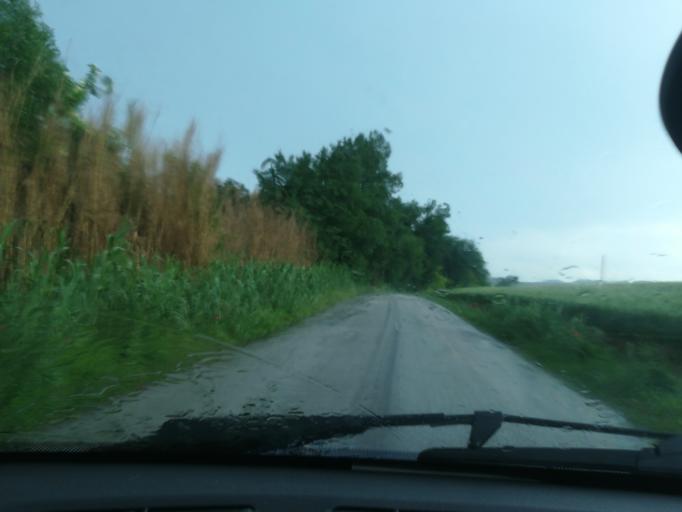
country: IT
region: The Marches
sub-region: Provincia di Macerata
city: Passo di Treia
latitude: 43.3021
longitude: 13.3446
